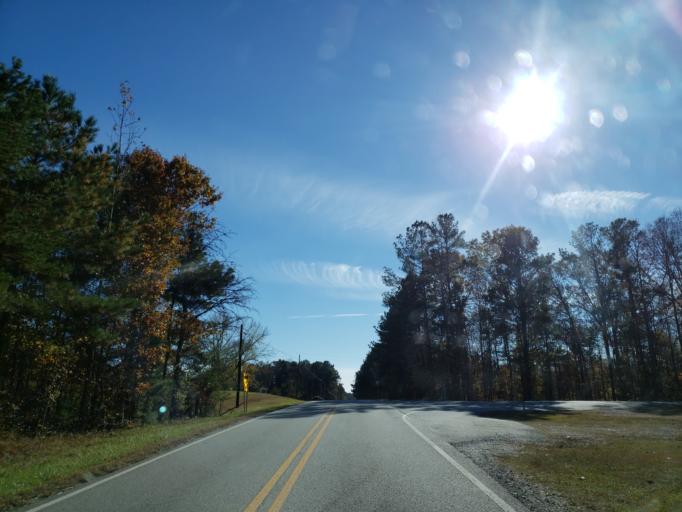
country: US
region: Alabama
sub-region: Cleburne County
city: Heflin
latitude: 33.5868
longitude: -85.6376
